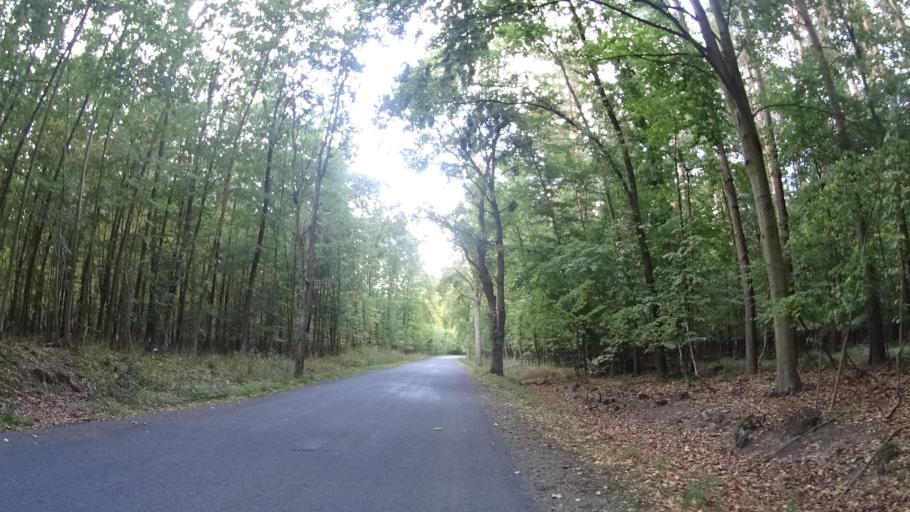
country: CZ
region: Olomoucky
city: Bila Lhota
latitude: 49.7291
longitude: 17.0114
